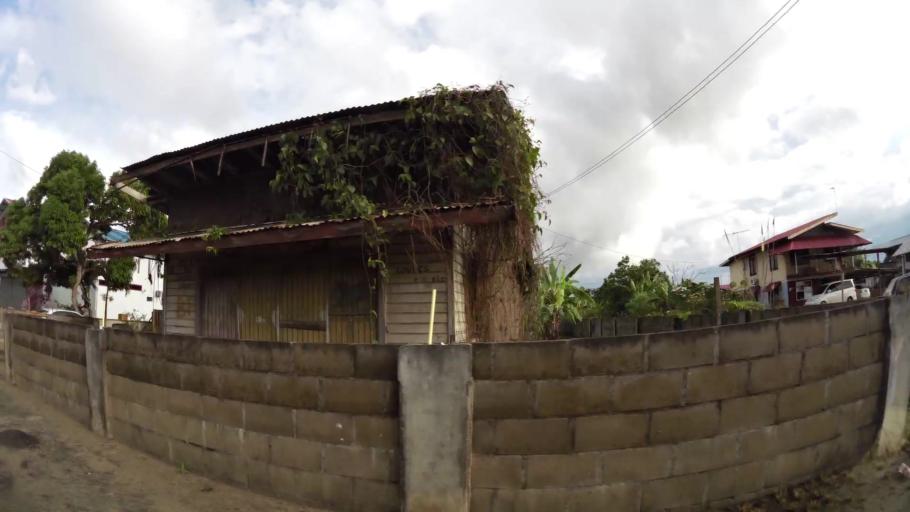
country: SR
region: Paramaribo
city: Paramaribo
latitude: 5.8469
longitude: -55.2365
